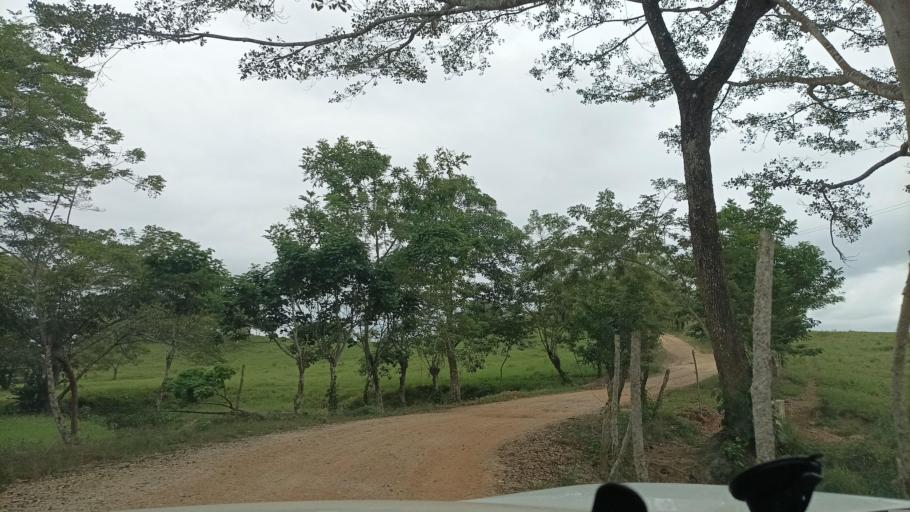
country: MX
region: Veracruz
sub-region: Uxpanapa
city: Poblado Cinco
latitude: 17.4928
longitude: -94.5677
